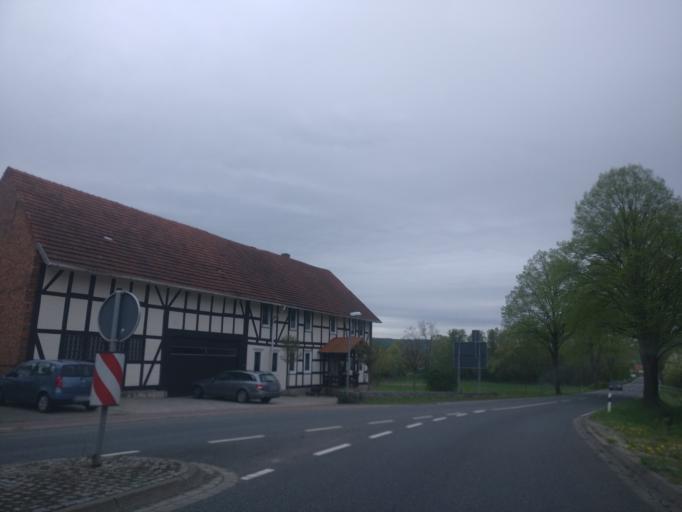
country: DE
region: Lower Saxony
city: Scheden
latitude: 51.4625
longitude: 9.7223
